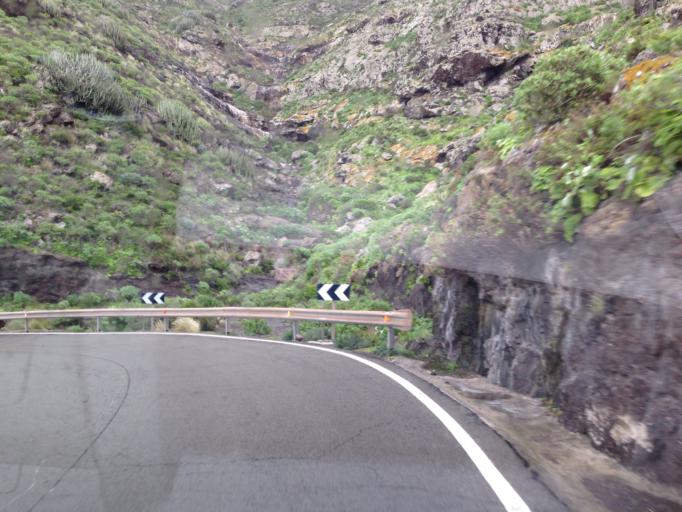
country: ES
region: Canary Islands
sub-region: Provincia de Las Palmas
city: San Nicolas
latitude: 28.0342
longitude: -15.7541
